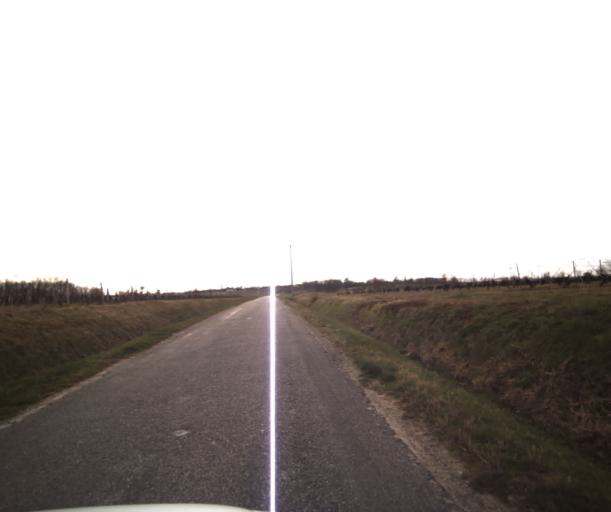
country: FR
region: Midi-Pyrenees
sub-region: Departement du Tarn-et-Garonne
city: Campsas
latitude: 43.8989
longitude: 1.3413
